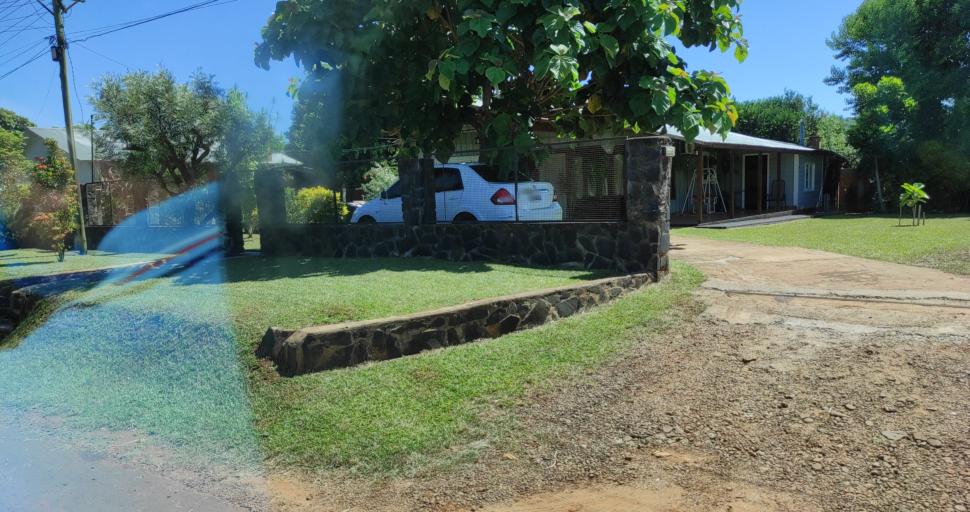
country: AR
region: Misiones
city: El Soberbio
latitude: -27.3018
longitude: -54.1939
